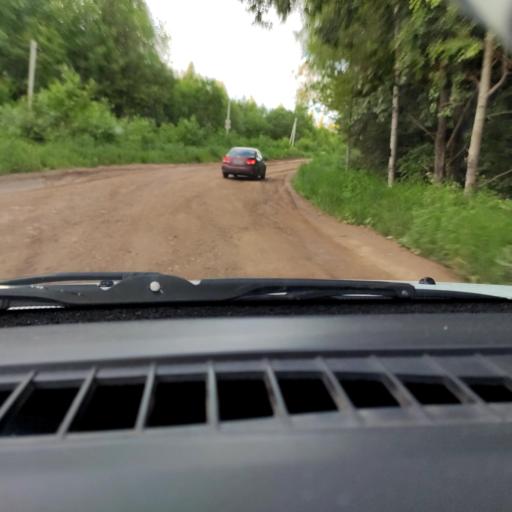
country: RU
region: Perm
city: Polazna
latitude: 58.2001
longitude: 56.4744
